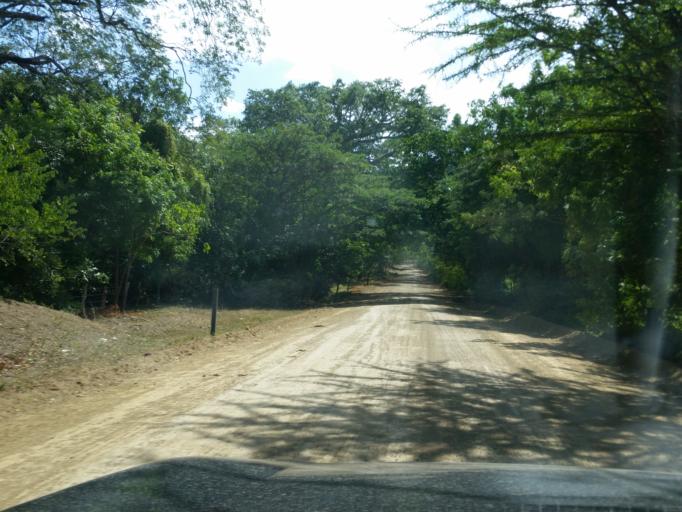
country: NI
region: Rivas
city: San Juan del Sur
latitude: 11.1385
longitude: -85.7833
